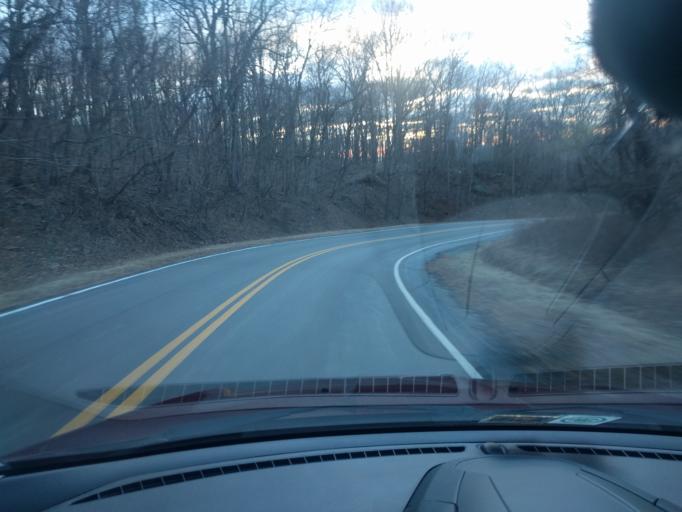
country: US
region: Virginia
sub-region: City of Bedford
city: Bedford
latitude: 37.4395
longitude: -79.5862
